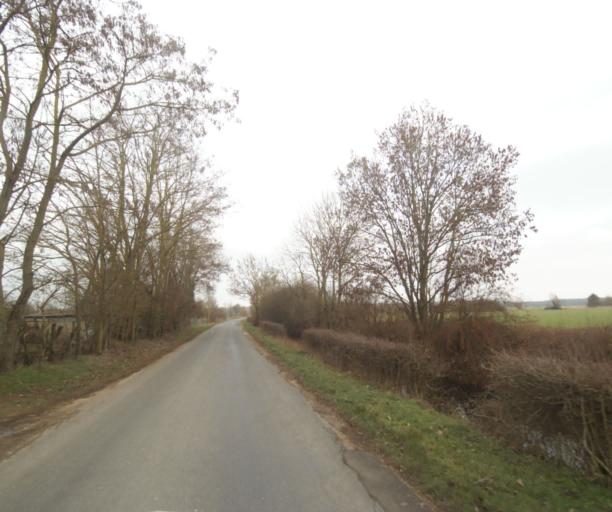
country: FR
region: Champagne-Ardenne
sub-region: Departement de la Haute-Marne
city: Villiers-en-Lieu
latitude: 48.6573
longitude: 4.8268
